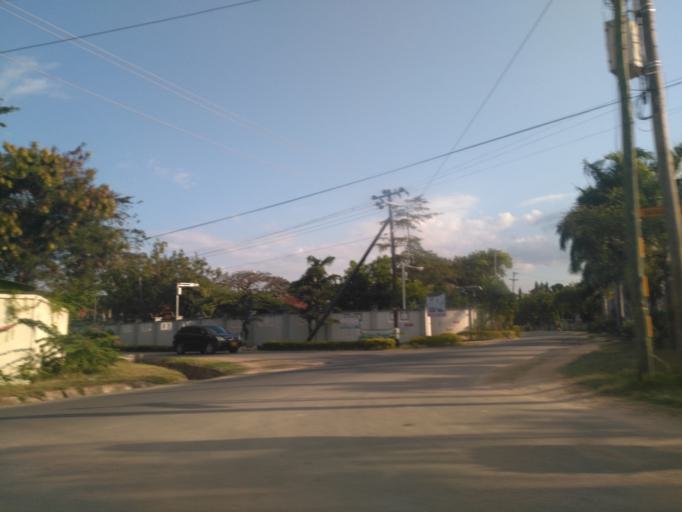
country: TZ
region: Dar es Salaam
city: Magomeni
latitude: -6.7811
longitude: 39.2723
